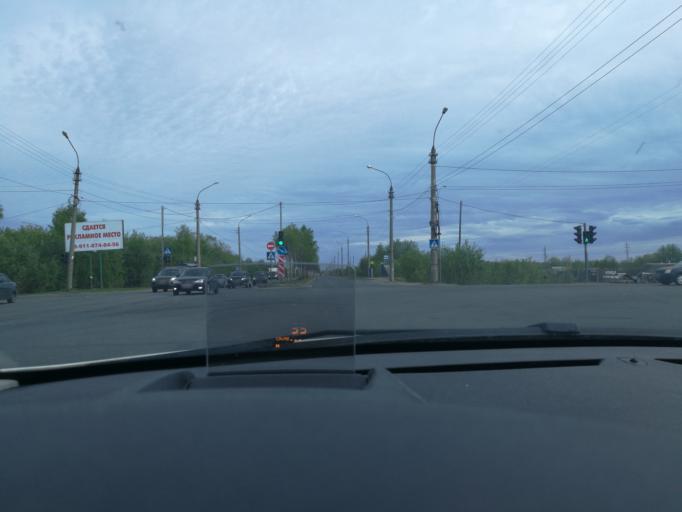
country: RU
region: Arkhangelskaya
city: Arkhangel'sk
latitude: 64.5981
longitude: 40.5255
